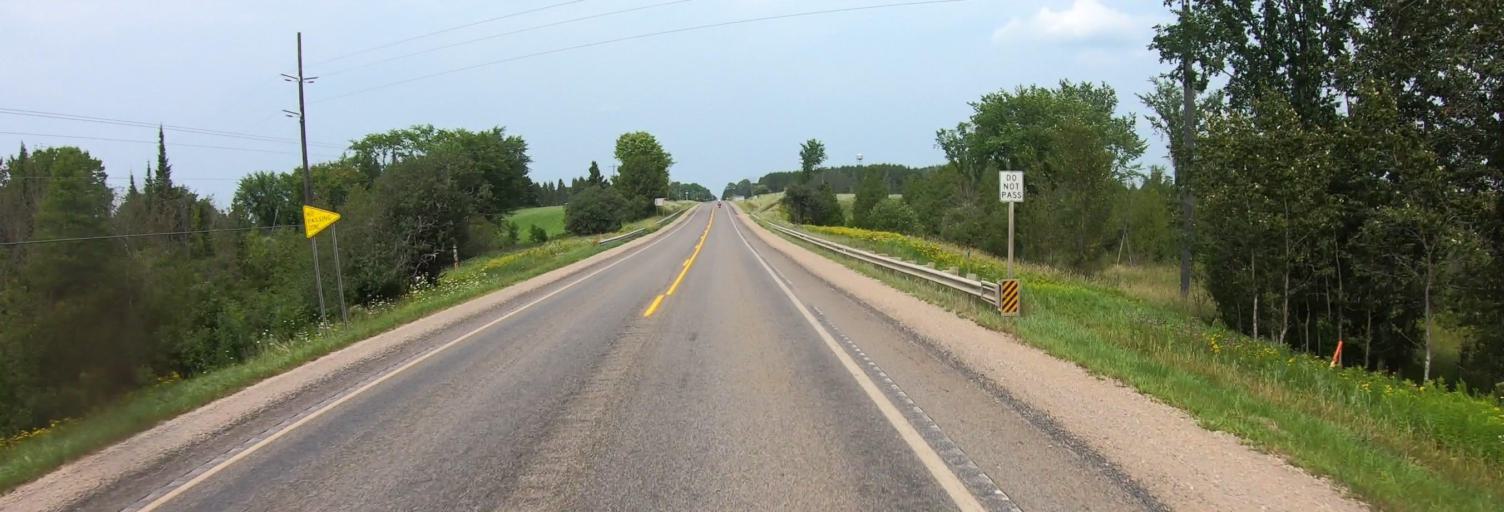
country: US
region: Michigan
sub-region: Alger County
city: Munising
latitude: 46.3367
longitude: -86.9289
